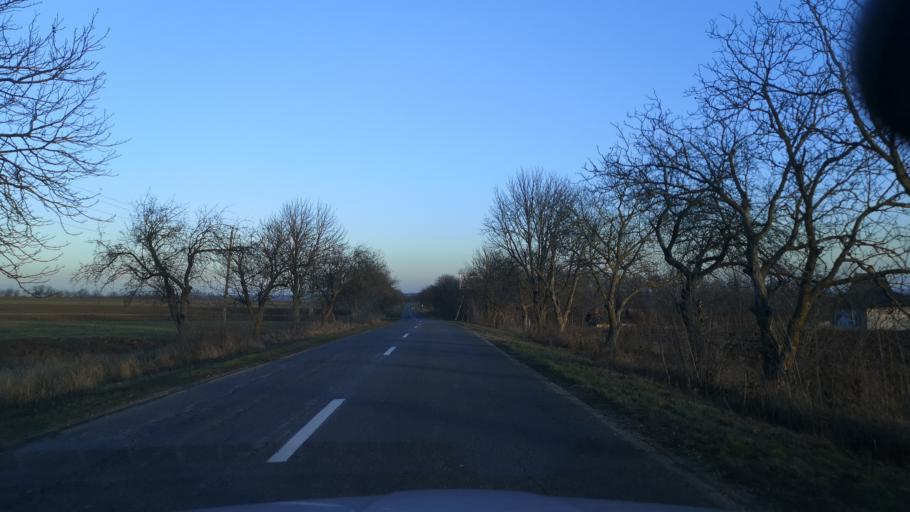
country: MD
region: Orhei
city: Orhei
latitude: 47.3118
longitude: 28.9507
